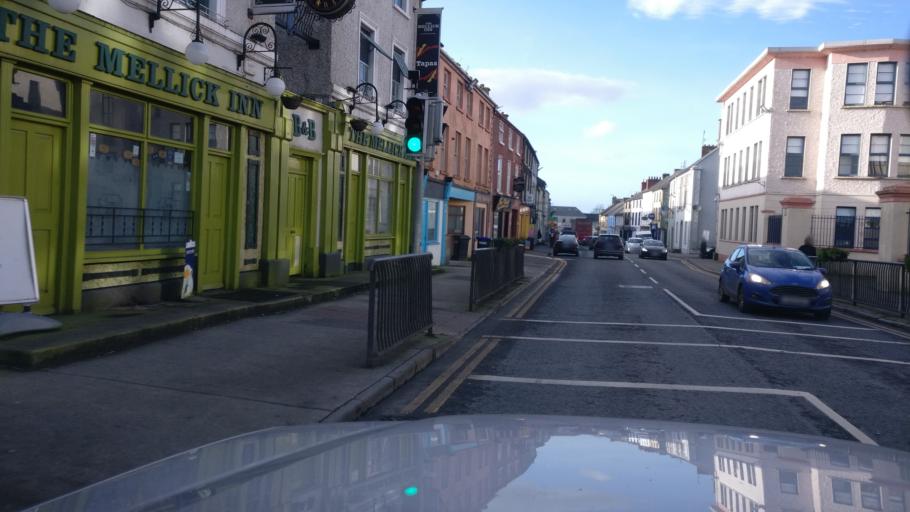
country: IE
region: Leinster
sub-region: Laois
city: Mountmellick
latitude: 53.1177
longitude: -7.3276
